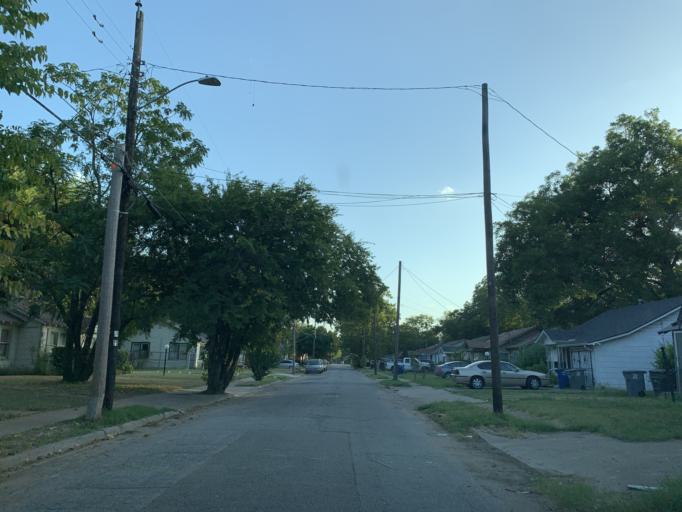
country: US
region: Texas
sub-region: Dallas County
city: Dallas
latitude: 32.7641
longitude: -96.7448
